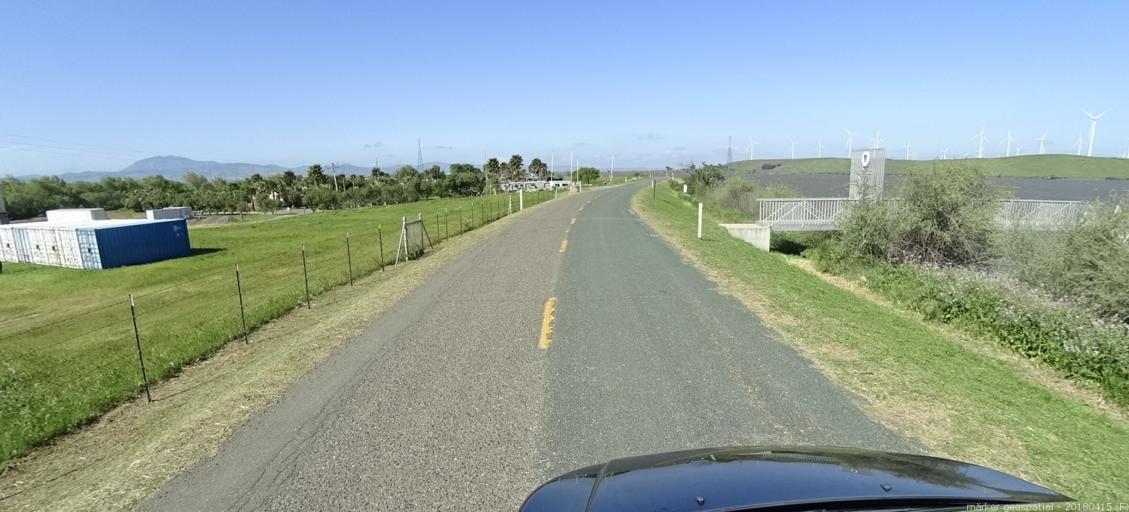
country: US
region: California
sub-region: Contra Costa County
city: Antioch
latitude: 38.0723
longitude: -121.7619
